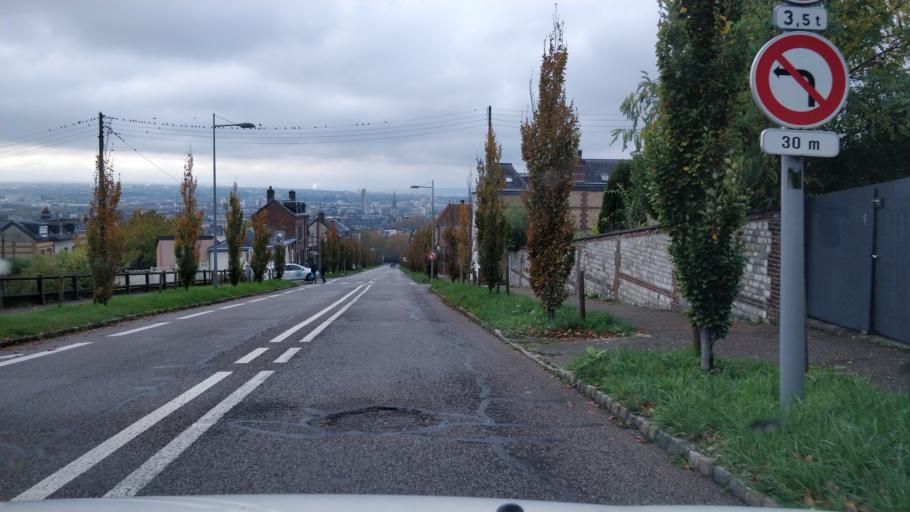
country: FR
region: Haute-Normandie
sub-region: Departement de la Seine-Maritime
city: Bihorel
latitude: 49.4488
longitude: 1.1131
